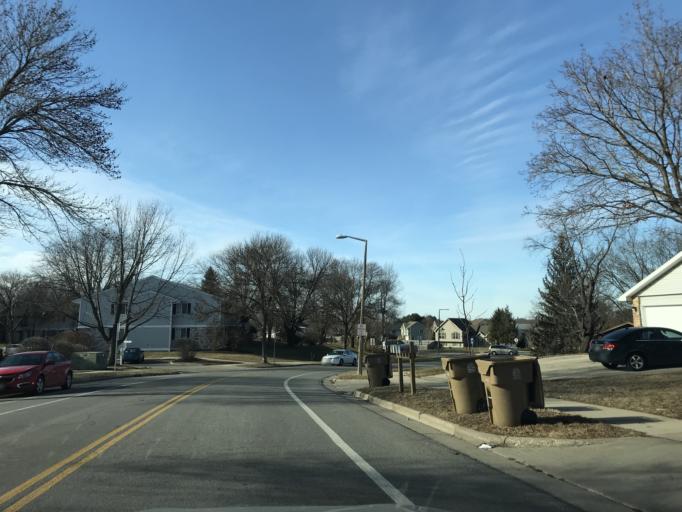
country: US
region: Wisconsin
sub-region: Dane County
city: Maple Bluff
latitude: 43.1424
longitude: -89.3050
